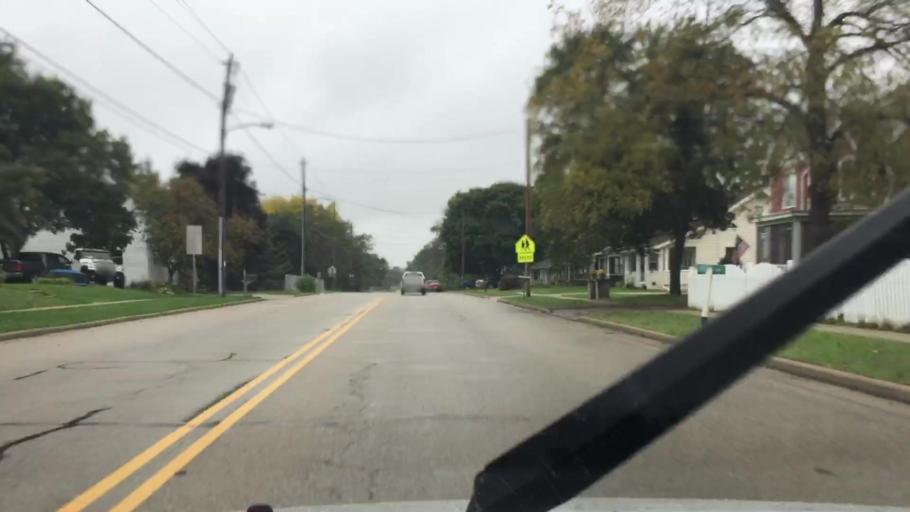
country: US
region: Wisconsin
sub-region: Jefferson County
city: Palmyra
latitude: 42.8788
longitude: -88.5911
